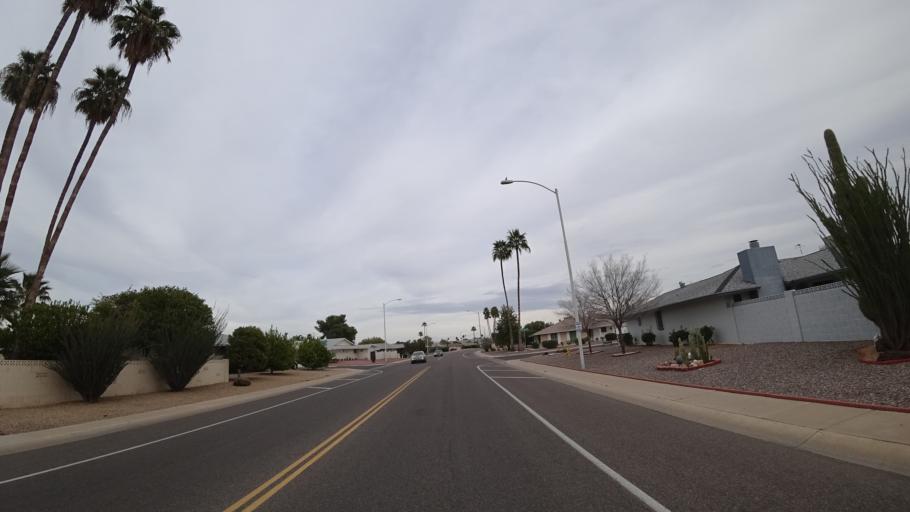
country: US
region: Arizona
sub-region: Maricopa County
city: Youngtown
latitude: 33.6163
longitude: -112.2965
